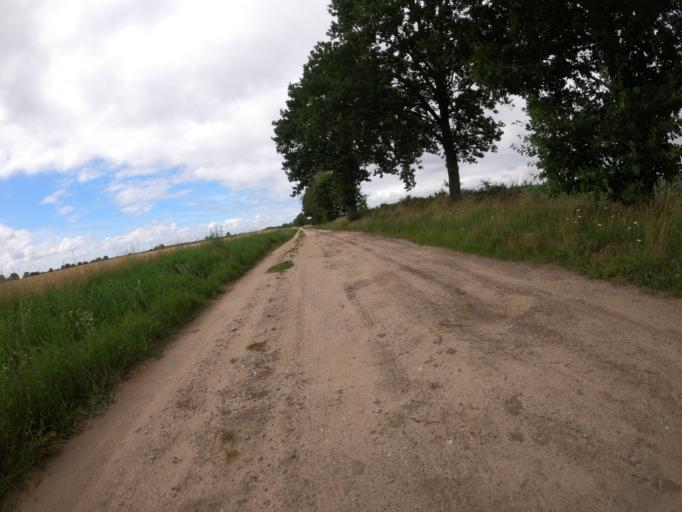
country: PL
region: West Pomeranian Voivodeship
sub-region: Powiat bialogardzki
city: Tychowo
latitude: 53.9951
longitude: 16.3788
